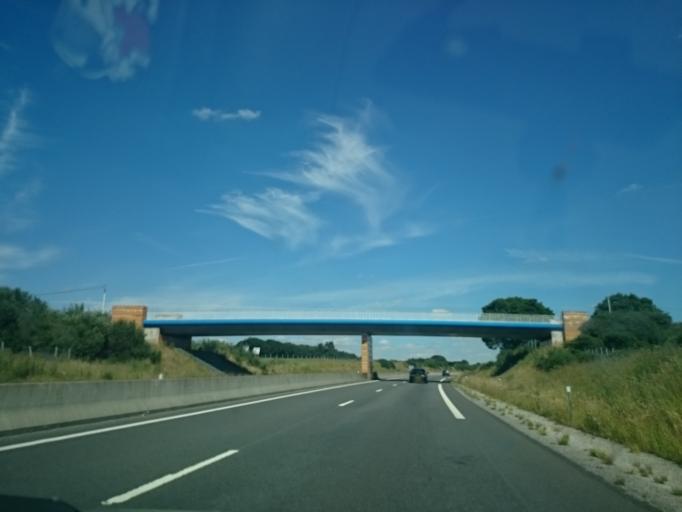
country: FR
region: Brittany
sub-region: Departement des Cotes-d'Armor
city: Gouarec
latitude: 48.2331
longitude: -3.1413
